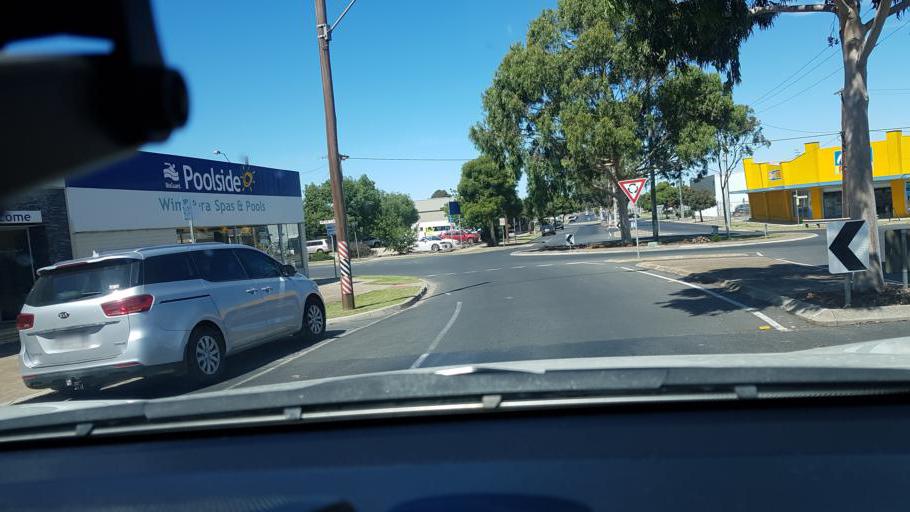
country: AU
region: Victoria
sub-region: Horsham
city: Horsham
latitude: -36.7161
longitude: 142.2024
